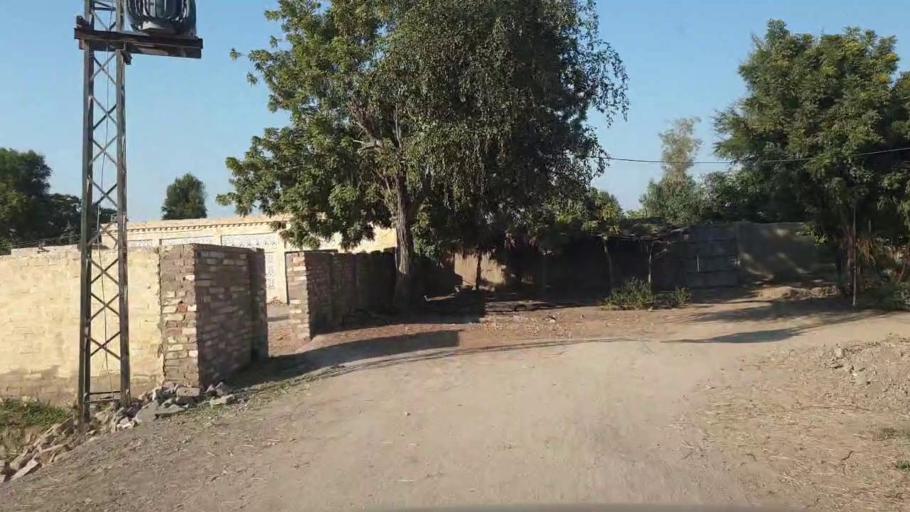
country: PK
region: Sindh
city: Shahpur Chakar
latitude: 26.1586
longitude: 68.6619
